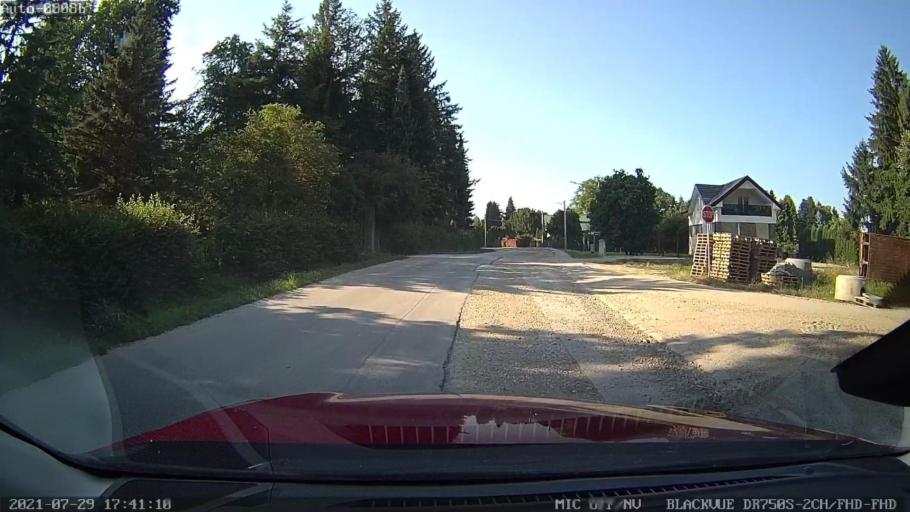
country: HR
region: Varazdinska
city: Vinica
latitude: 46.3261
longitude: 16.1514
